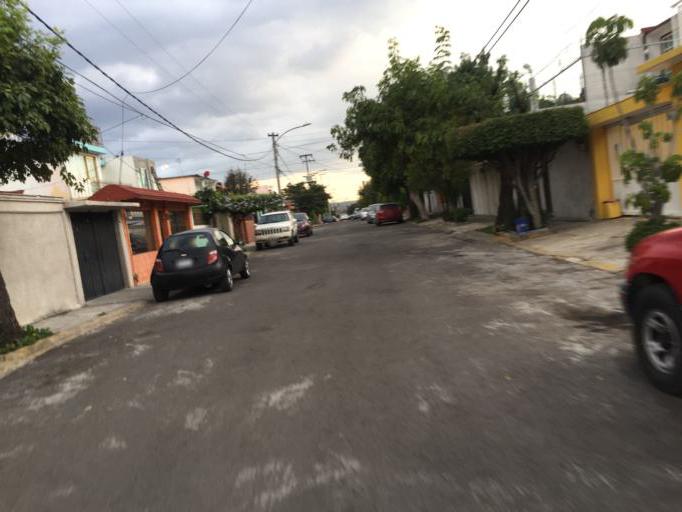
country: MX
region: Mexico
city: Cuautitlan Izcalli
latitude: 19.6528
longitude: -99.2105
